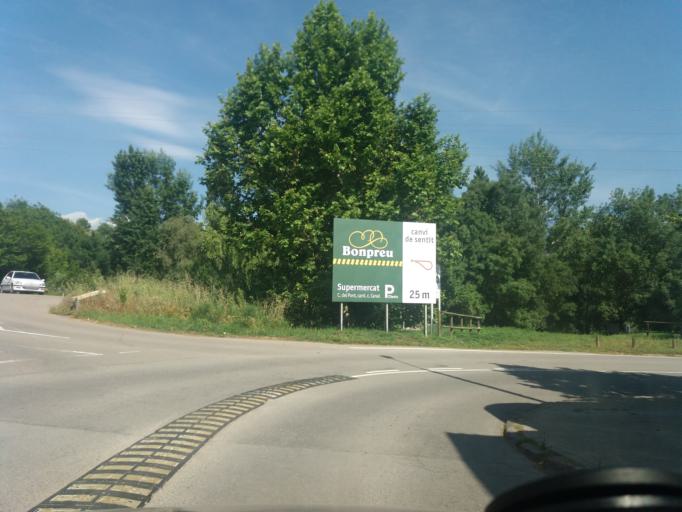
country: ES
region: Catalonia
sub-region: Provincia de Barcelona
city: Sant Joan de Vilatorrada
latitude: 41.7453
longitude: 1.8086
